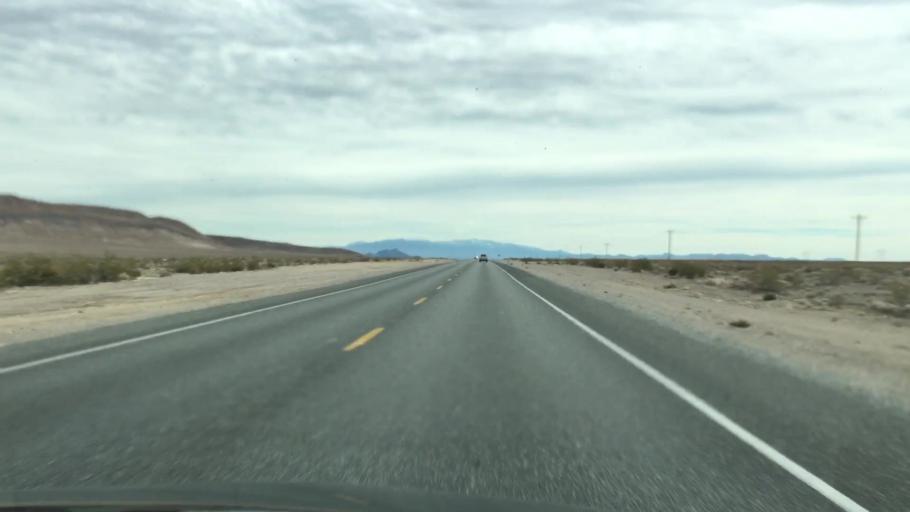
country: US
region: Nevada
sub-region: Nye County
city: Beatty
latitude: 36.6937
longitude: -116.5696
